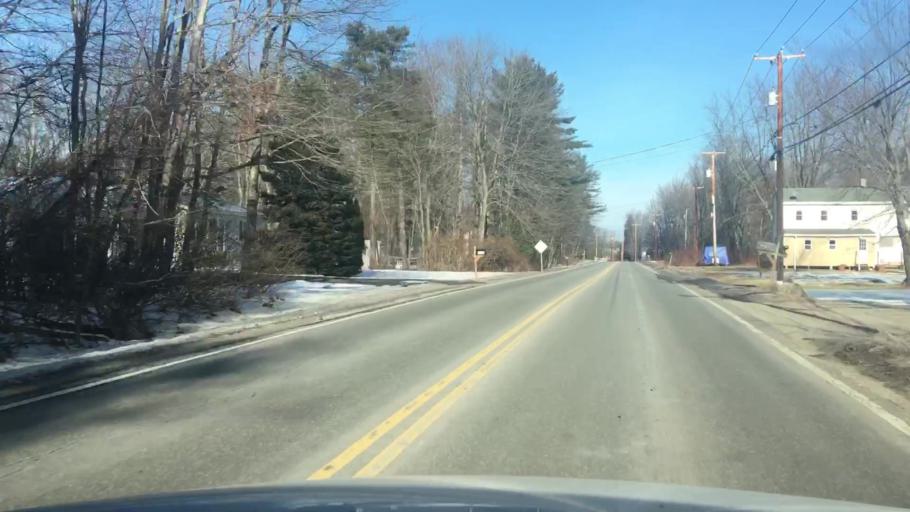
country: US
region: Maine
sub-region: Androscoggin County
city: Auburn
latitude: 44.0900
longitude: -70.2629
